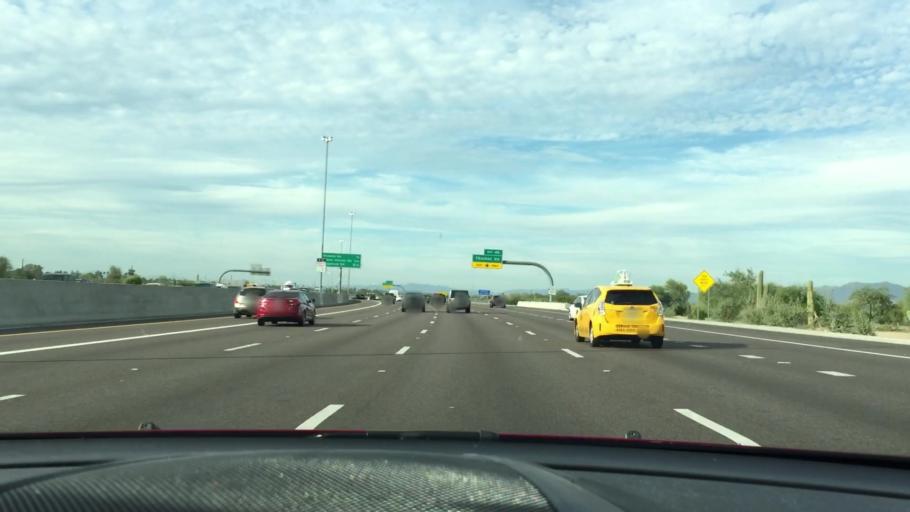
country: US
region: Arizona
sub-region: Maricopa County
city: Scottsdale
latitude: 33.4719
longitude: -111.8876
